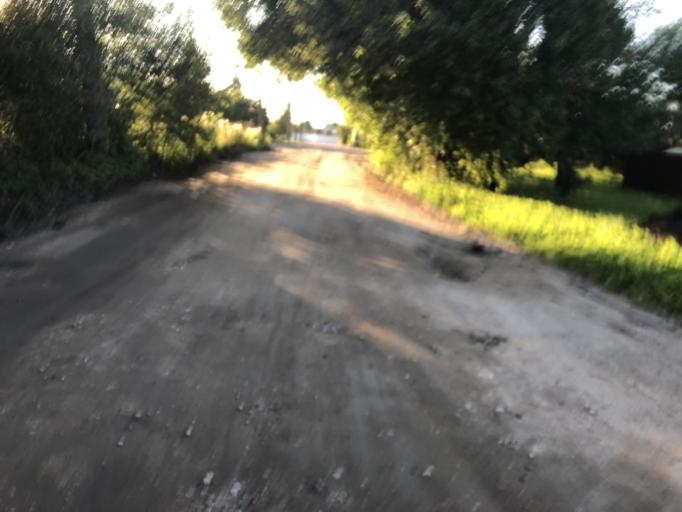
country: RU
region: Tverskaya
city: Rzhev
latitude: 56.2453
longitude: 34.3033
